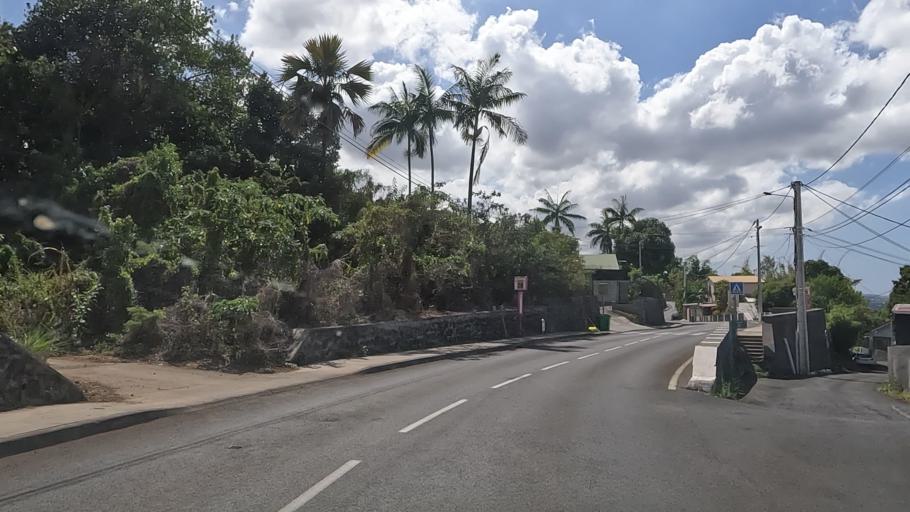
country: RE
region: Reunion
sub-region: Reunion
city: L'Entre-Deux
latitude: -21.2589
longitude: 55.4425
